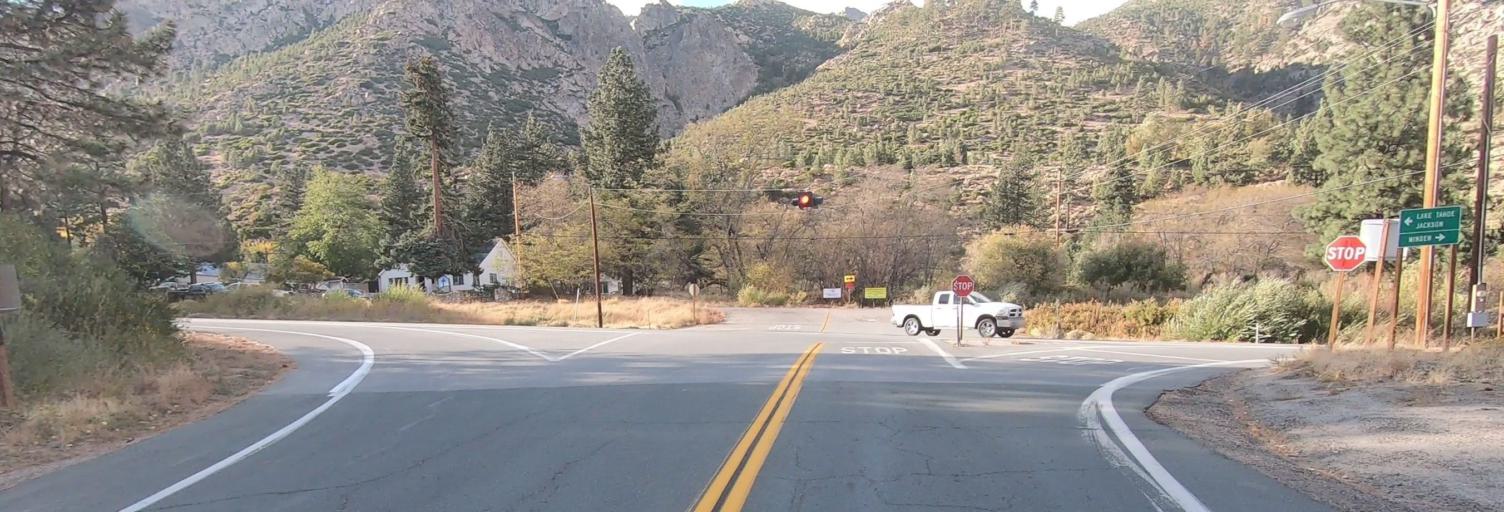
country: US
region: Nevada
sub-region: Douglas County
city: Gardnerville Ranchos
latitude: 38.7746
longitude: -119.8236
